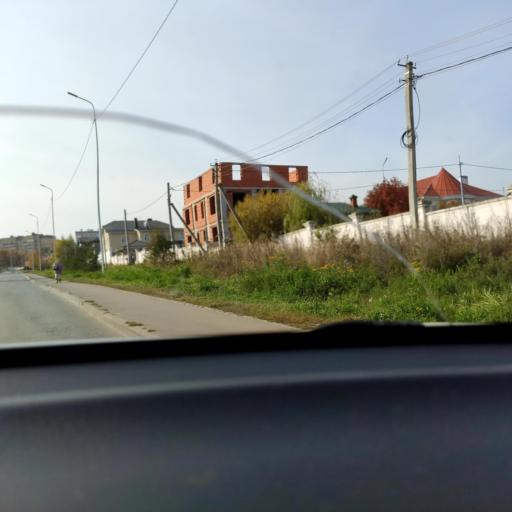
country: RU
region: Tatarstan
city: Stolbishchi
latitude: 55.7630
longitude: 49.2443
